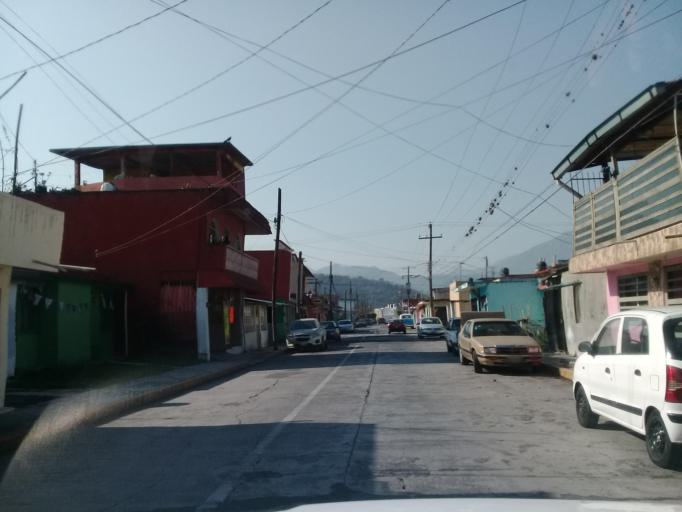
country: MX
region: Veracruz
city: Ixtac Zoquitlan
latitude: 18.8555
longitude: -97.0684
